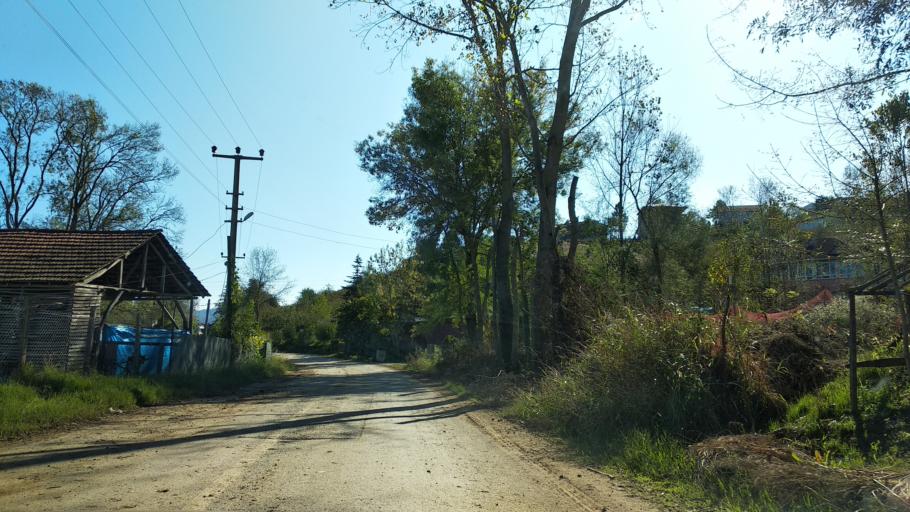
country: TR
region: Sakarya
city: Ortakoy
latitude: 41.0340
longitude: 30.5952
